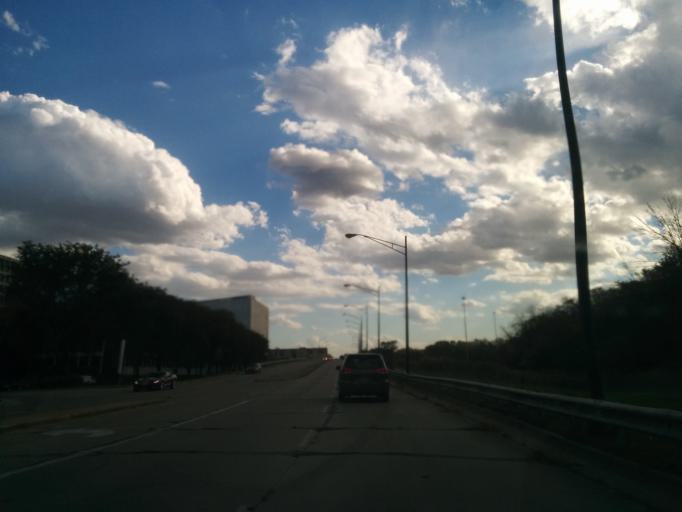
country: US
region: Illinois
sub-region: Cook County
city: Park Ridge
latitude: 41.9869
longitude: -87.8466
